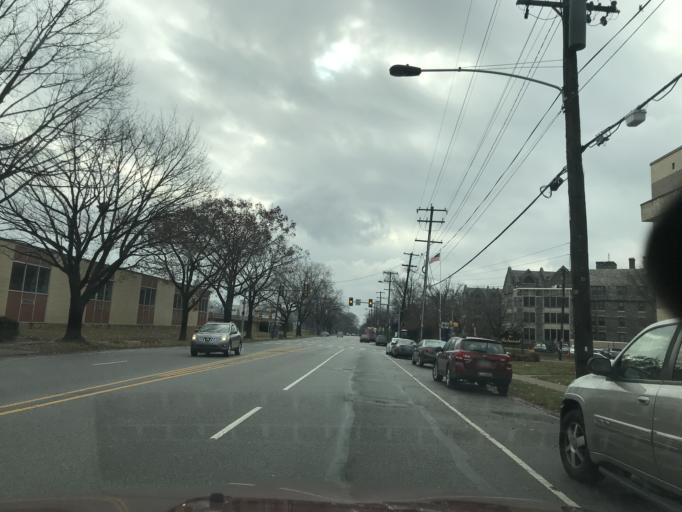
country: US
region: Pennsylvania
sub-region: Montgomery County
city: Bala-Cynwyd
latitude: 40.0005
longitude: -75.2198
